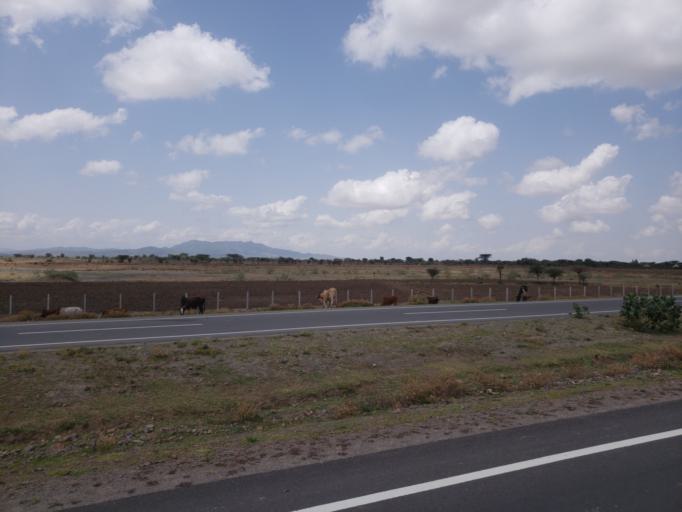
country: ET
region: Oromiya
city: Mojo
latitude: 8.2860
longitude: 38.9189
